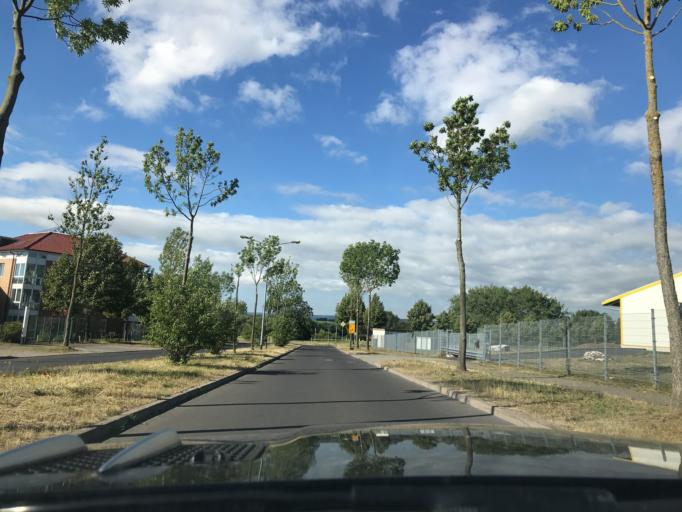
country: DE
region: Thuringia
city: Muehlhausen
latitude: 51.1956
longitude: 10.4717
